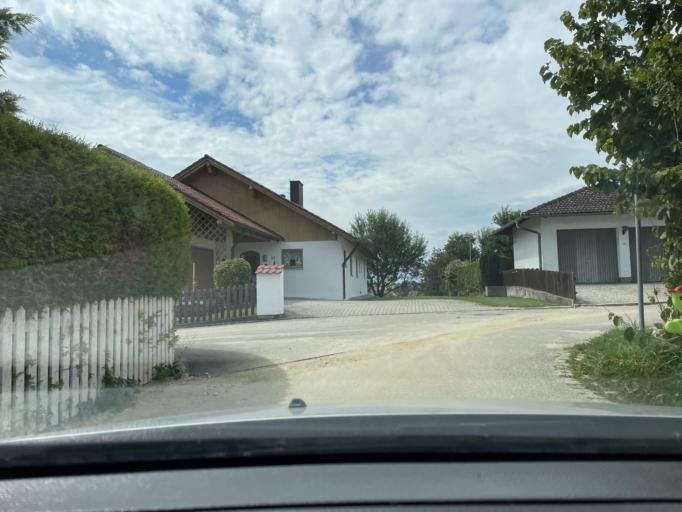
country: DE
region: Bavaria
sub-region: Lower Bavaria
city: Altfraunhofen
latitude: 48.4466
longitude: 12.1738
